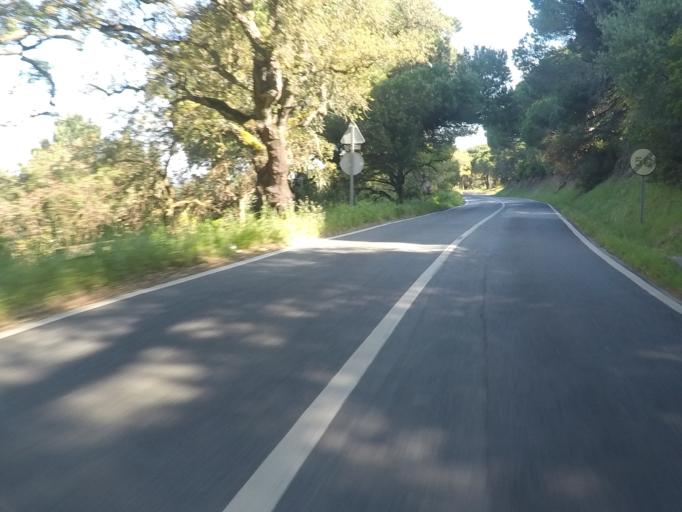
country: PT
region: Setubal
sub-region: Sesimbra
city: Sesimbra
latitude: 38.5062
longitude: -9.1478
